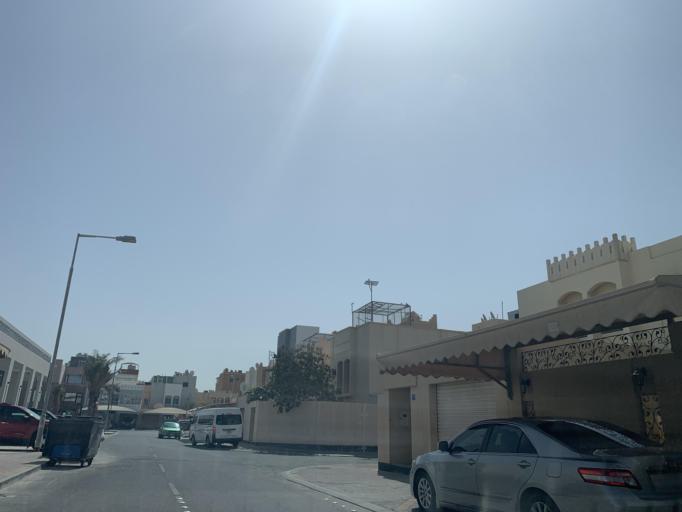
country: BH
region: Muharraq
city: Al Muharraq
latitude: 26.2693
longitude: 50.5966
